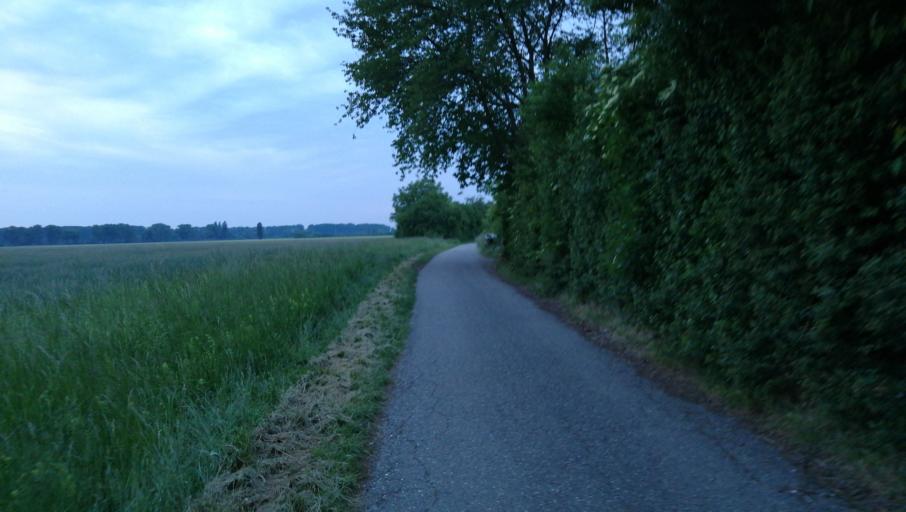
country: DE
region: Baden-Wuerttemberg
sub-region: Karlsruhe Region
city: Altlussheim
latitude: 49.3274
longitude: 8.4912
